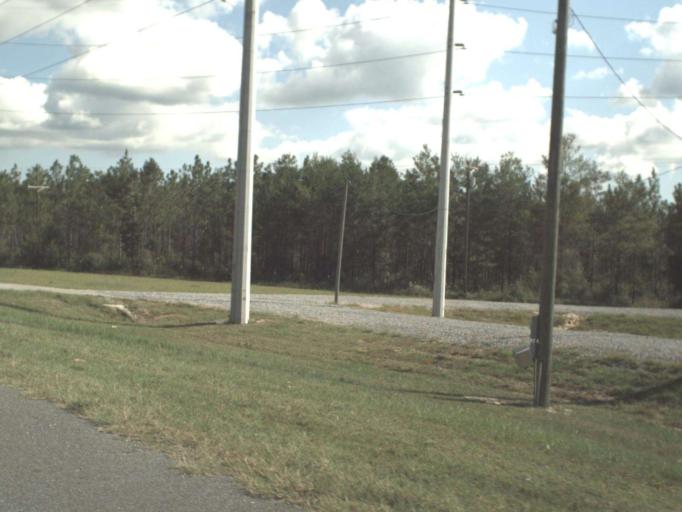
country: US
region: Florida
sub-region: Bay County
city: Laguna Beach
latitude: 30.4415
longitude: -85.8701
